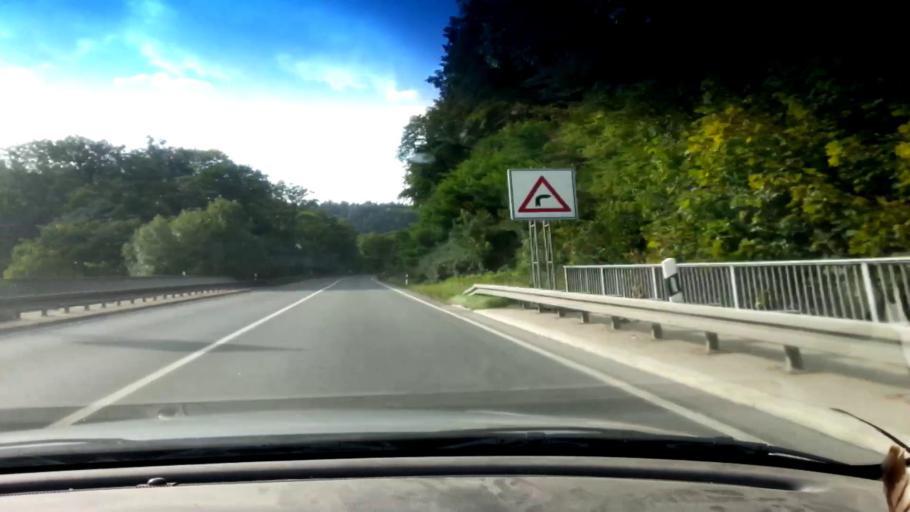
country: DE
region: Bavaria
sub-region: Upper Franconia
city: Goldkronach
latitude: 50.0283
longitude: 11.6896
